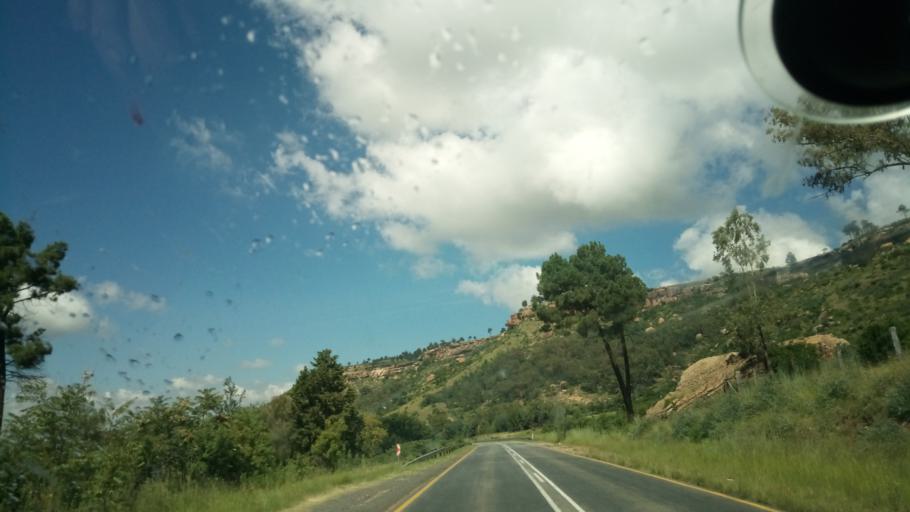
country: ZA
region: Orange Free State
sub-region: Thabo Mofutsanyana District Municipality
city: Ficksburg
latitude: -28.8640
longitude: 27.8728
